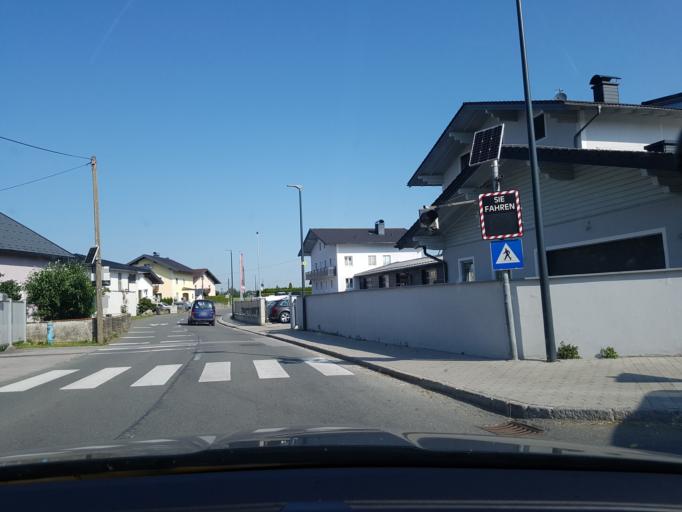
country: DE
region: Bavaria
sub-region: Upper Bavaria
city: Ainring
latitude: 47.7777
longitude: 12.9901
